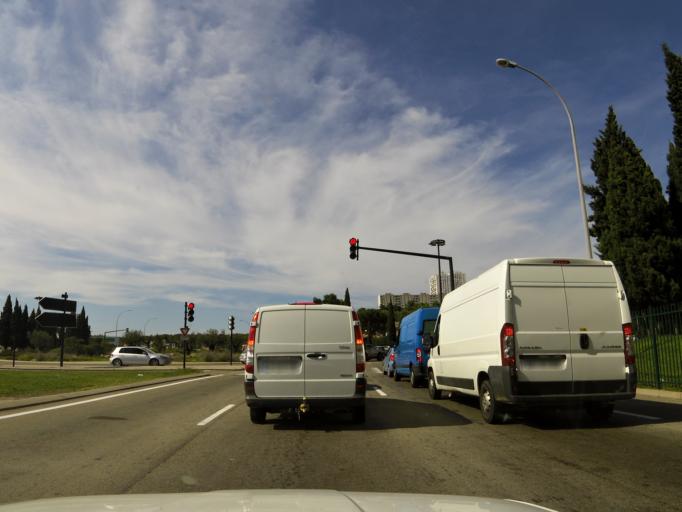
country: FR
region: Languedoc-Roussillon
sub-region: Departement du Gard
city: Nimes
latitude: 43.8230
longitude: 4.3284
